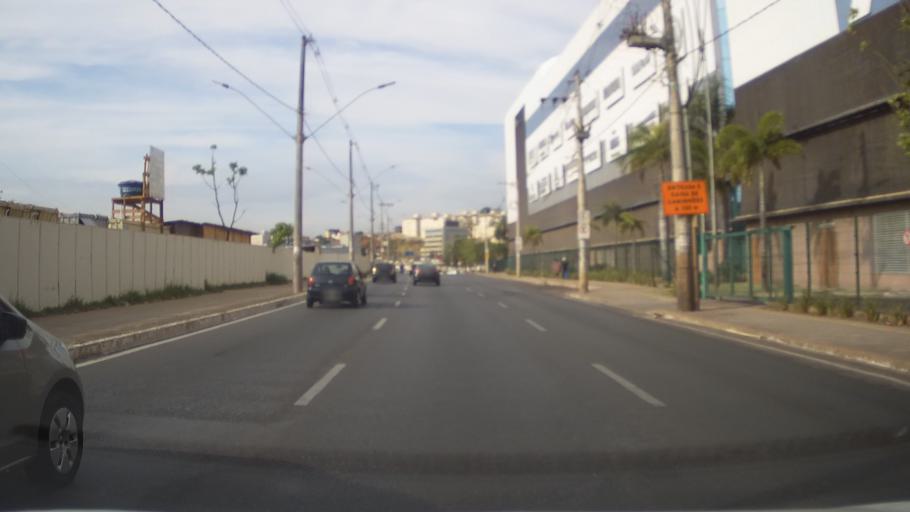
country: BR
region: Minas Gerais
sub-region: Contagem
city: Contagem
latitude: -19.8809
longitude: -44.0378
